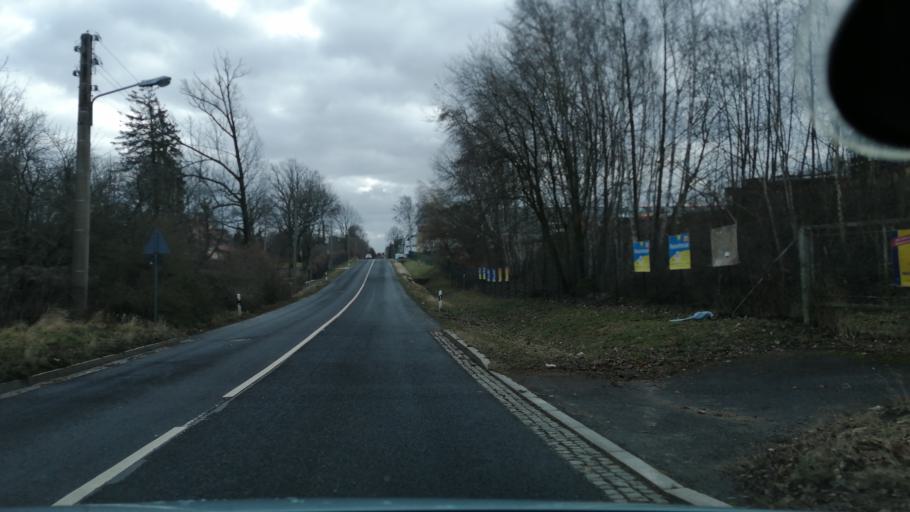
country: DE
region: Saxony
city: Lobau
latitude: 51.1033
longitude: 14.6551
